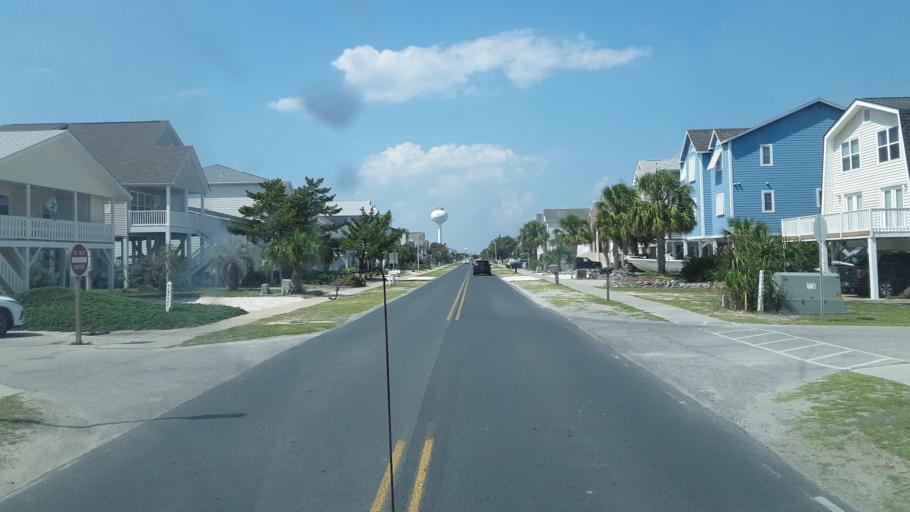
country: US
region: North Carolina
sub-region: Brunswick County
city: Sunset Beach
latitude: 33.8910
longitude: -78.4260
